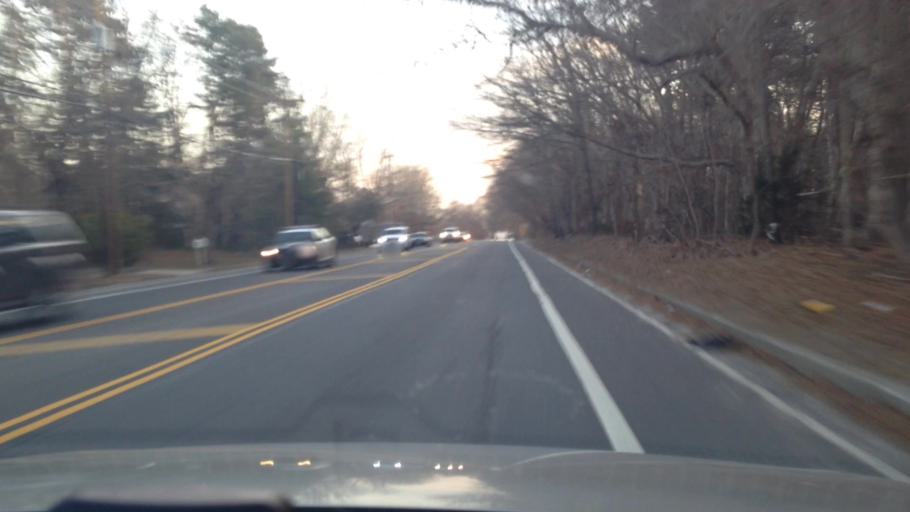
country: US
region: New York
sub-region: Suffolk County
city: Selden
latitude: 40.8794
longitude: -73.0272
